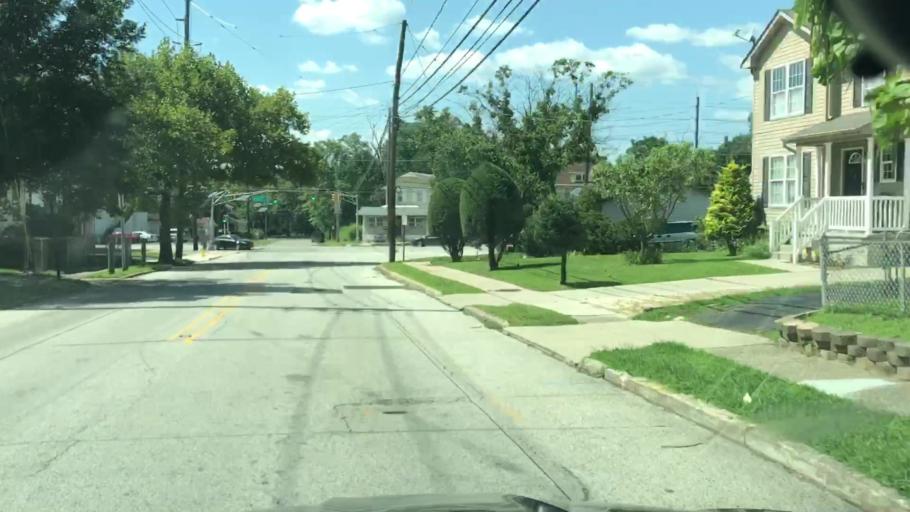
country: US
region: New Jersey
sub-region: Camden County
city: Pennsauken
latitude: 39.9818
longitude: -75.0507
